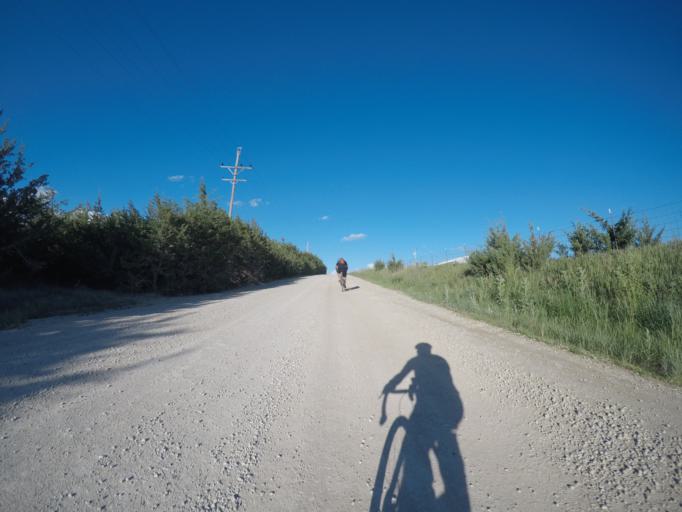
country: US
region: Kansas
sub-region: Riley County
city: Manhattan
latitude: 39.2616
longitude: -96.6863
